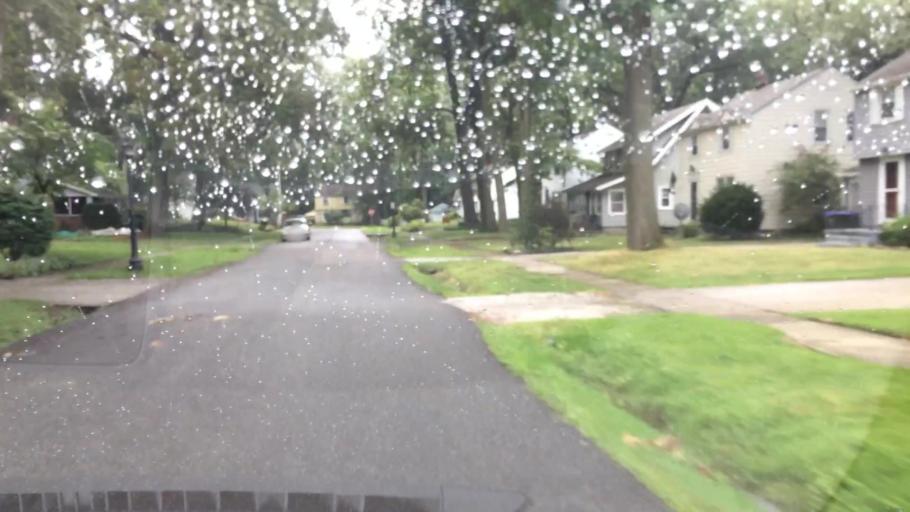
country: US
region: Ohio
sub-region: Summit County
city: Silver Lake
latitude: 41.1468
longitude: -81.4649
